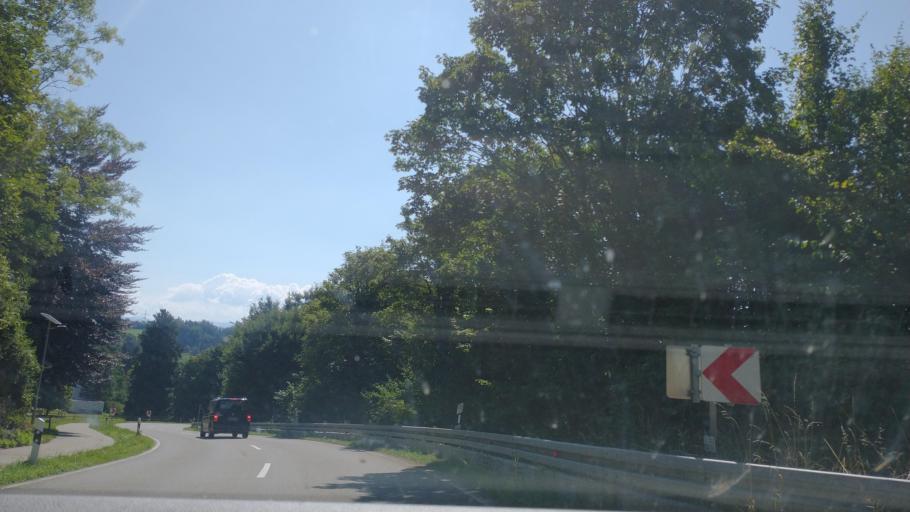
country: DE
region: Bavaria
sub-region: Swabia
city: Hergensweiler
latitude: 47.6551
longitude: 9.7752
